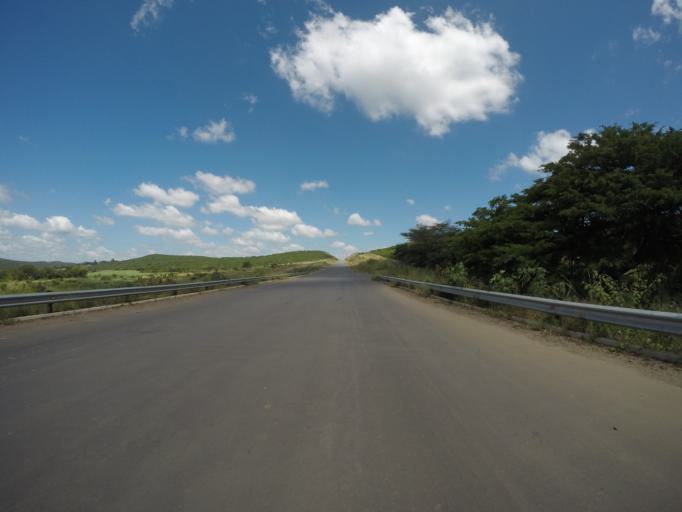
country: ZA
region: KwaZulu-Natal
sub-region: uThungulu District Municipality
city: Empangeni
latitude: -28.6191
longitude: 31.7560
